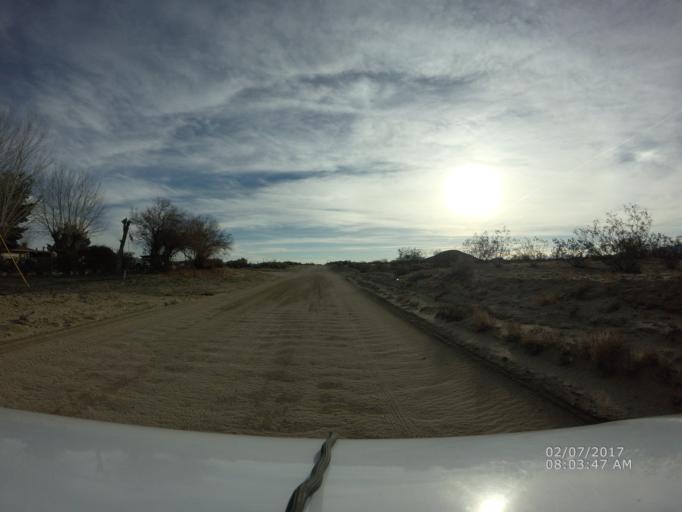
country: US
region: California
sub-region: Los Angeles County
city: Lake Los Angeles
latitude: 34.5726
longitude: -117.7629
